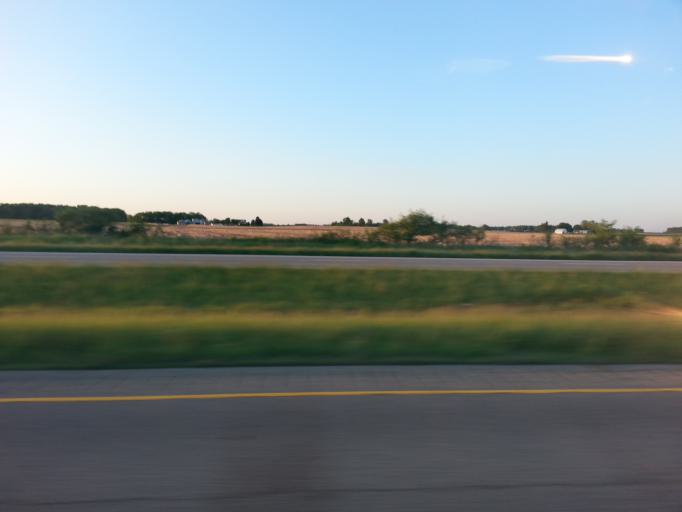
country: US
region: Indiana
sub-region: Fountain County
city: Veedersburg
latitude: 40.1130
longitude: -87.1066
